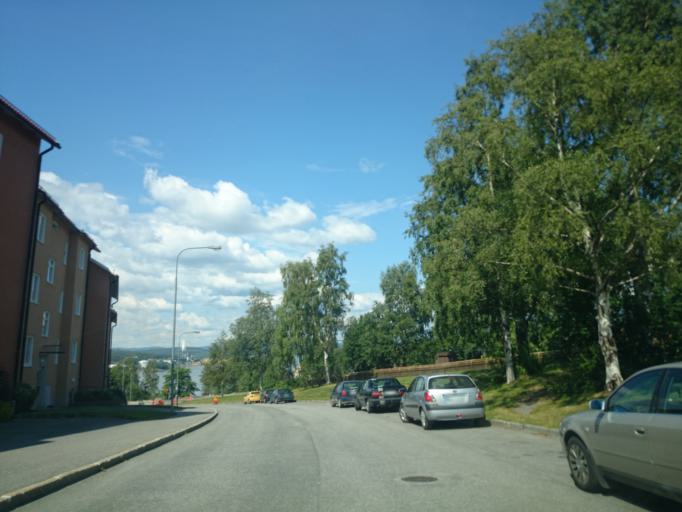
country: SE
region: Vaesternorrland
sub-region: Haernoesands Kommun
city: Haernoesand
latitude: 62.6374
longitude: 17.9539
